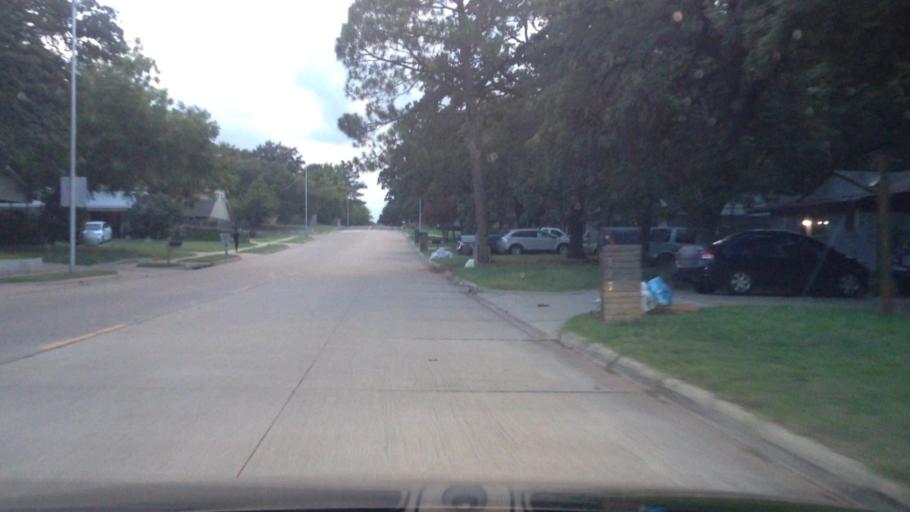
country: US
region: Texas
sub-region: Tarrant County
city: Arlington
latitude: 32.7429
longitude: -97.1356
